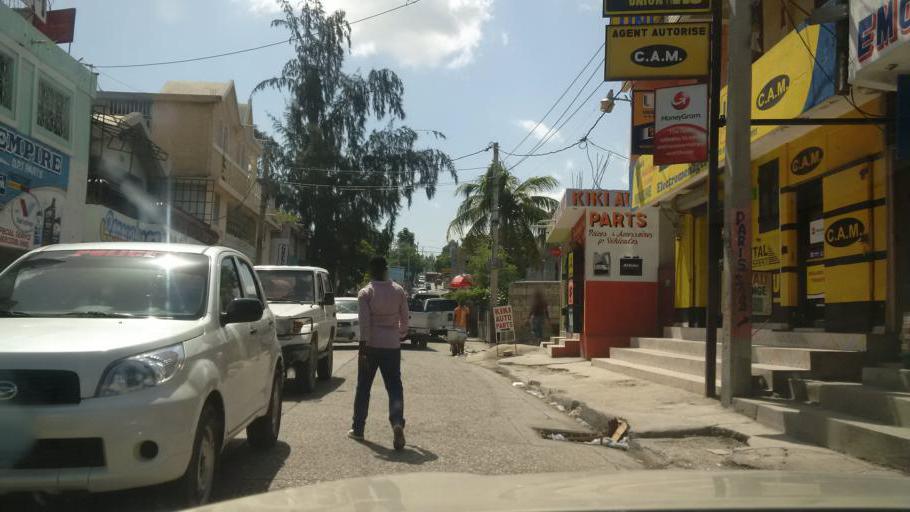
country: HT
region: Ouest
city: Delmas 73
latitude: 18.5549
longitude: -72.3137
